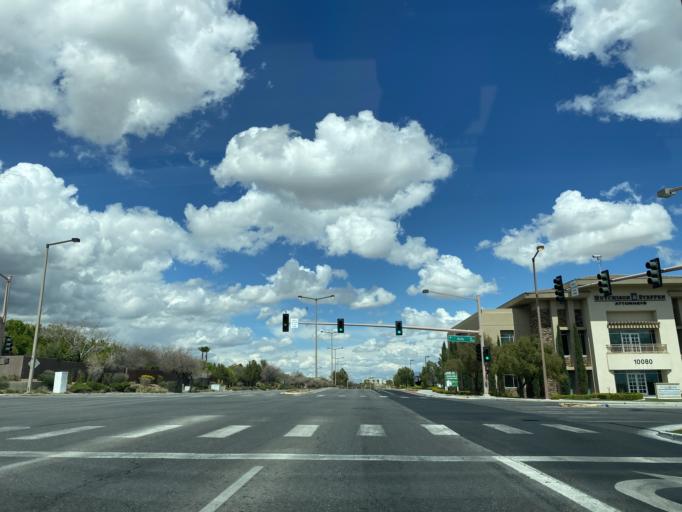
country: US
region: Nevada
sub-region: Clark County
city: Summerlin South
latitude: 36.1678
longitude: -115.3151
